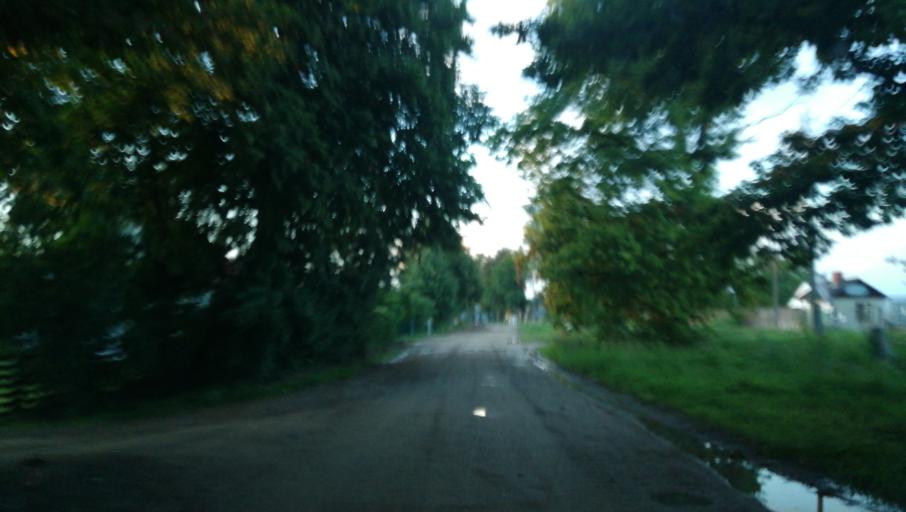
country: LV
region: Cesu Rajons
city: Cesis
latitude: 57.3190
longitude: 25.2964
